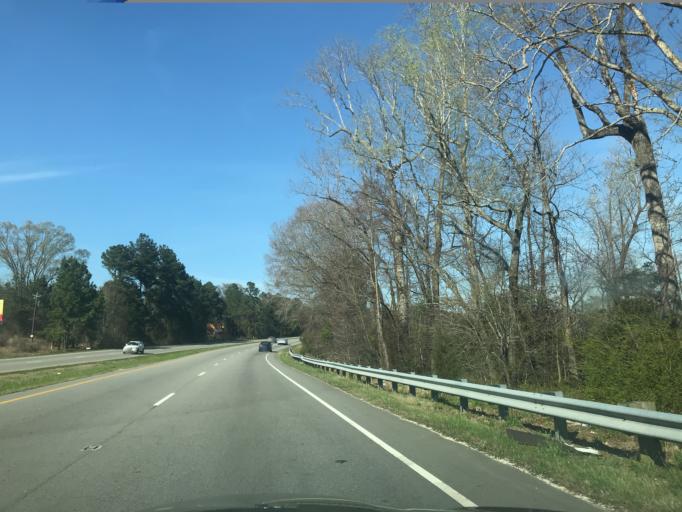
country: US
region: North Carolina
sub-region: Wake County
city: Garner
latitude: 35.6740
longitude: -78.6899
